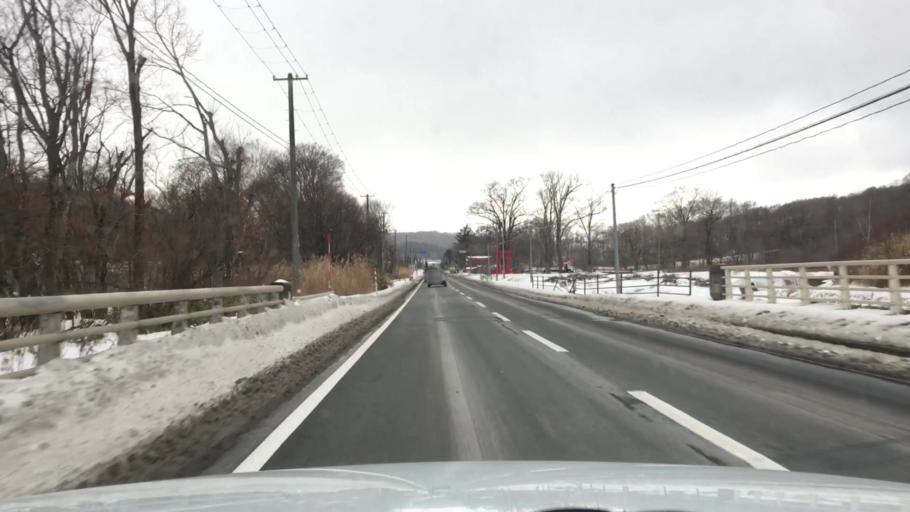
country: JP
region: Iwate
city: Morioka-shi
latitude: 39.6444
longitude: 141.3712
